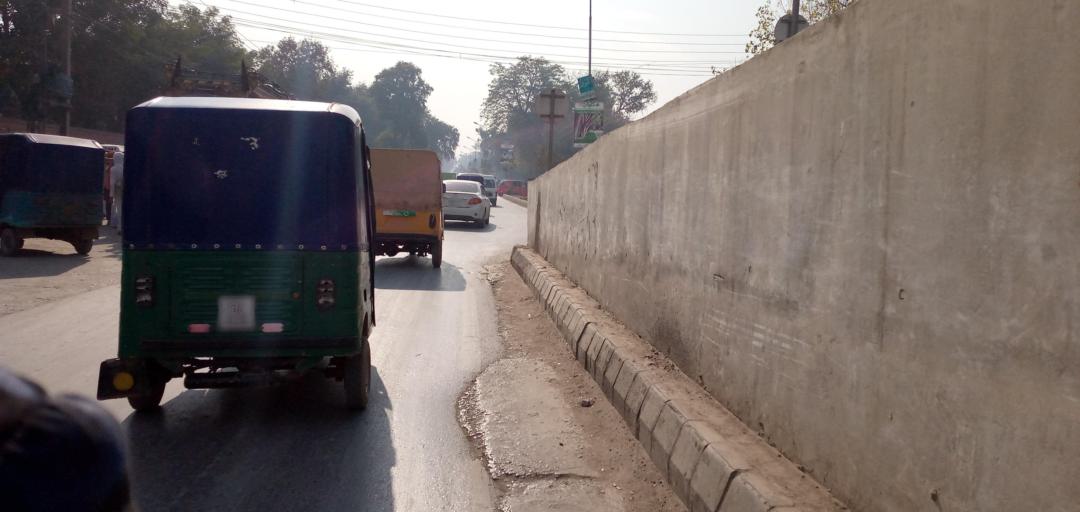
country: PK
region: Khyber Pakhtunkhwa
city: Peshawar
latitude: 33.9949
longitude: 71.5346
